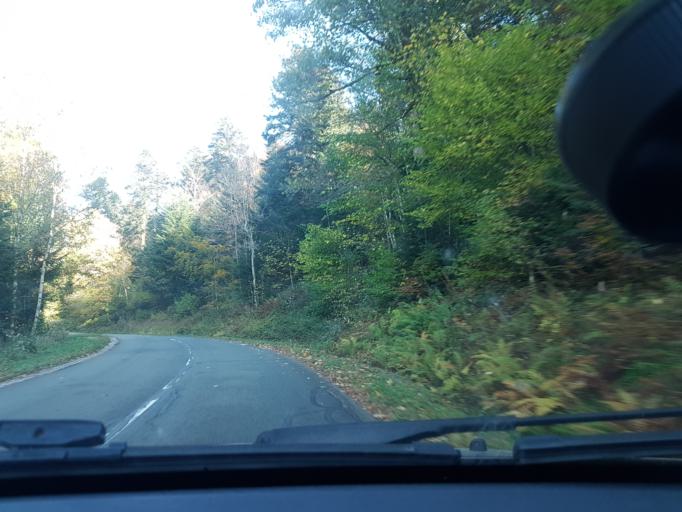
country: FR
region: Franche-Comte
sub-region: Departement de la Haute-Saone
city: Plancher-les-Mines
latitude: 47.7738
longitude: 6.7697
